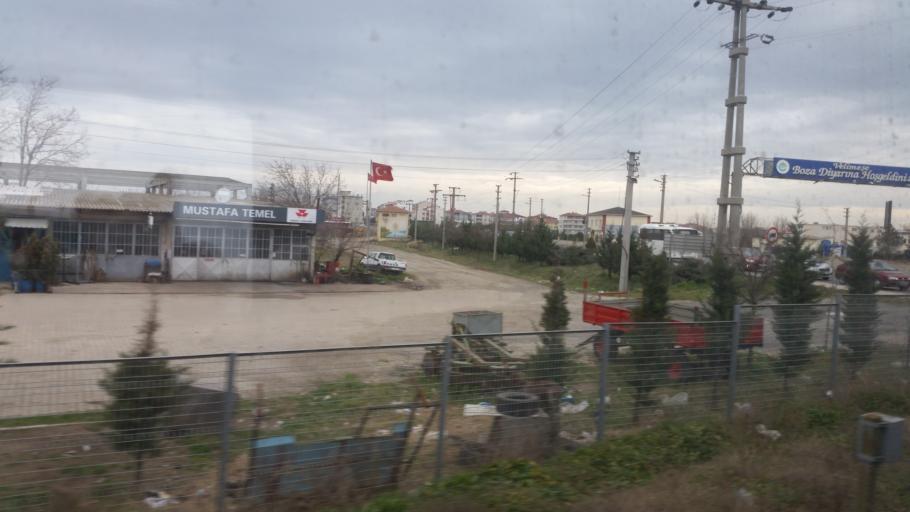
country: TR
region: Tekirdag
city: Velimese
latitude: 41.2436
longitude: 27.8832
